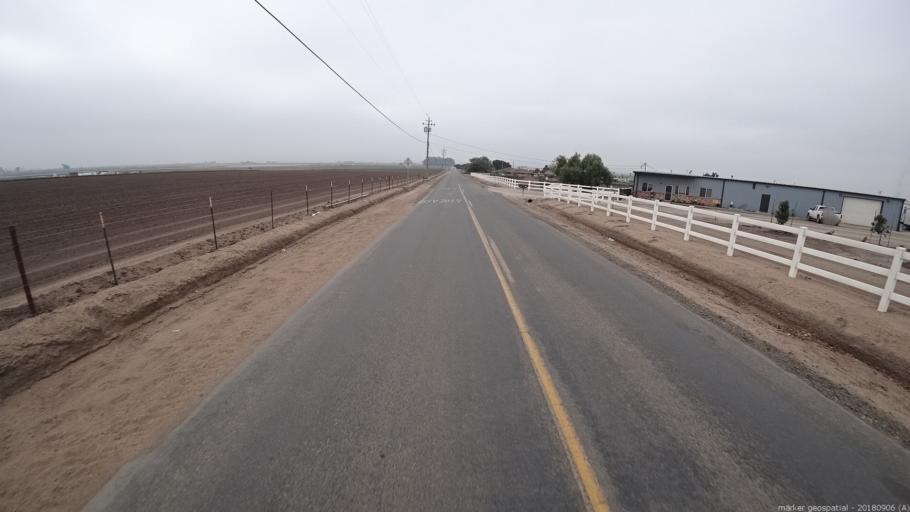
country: US
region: California
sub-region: Monterey County
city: Chualar
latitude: 36.6647
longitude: -121.5508
